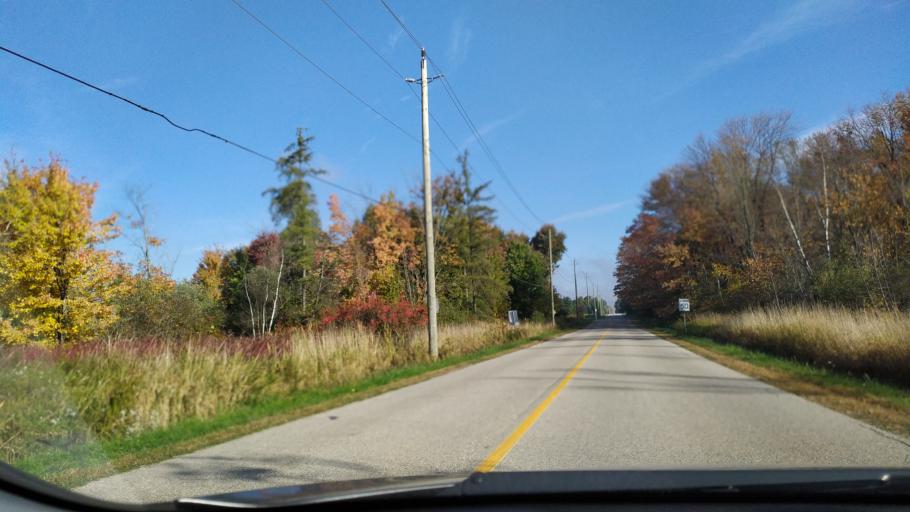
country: CA
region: Ontario
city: Waterloo
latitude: 43.5006
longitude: -80.6558
